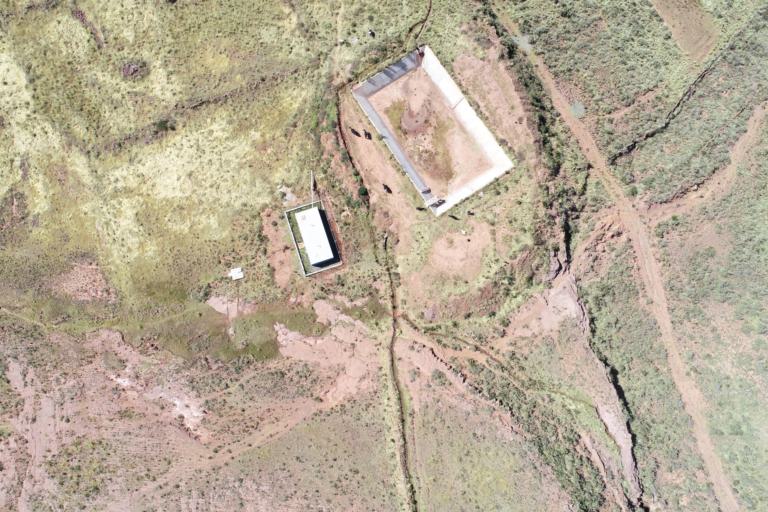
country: BO
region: La Paz
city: Tiahuanaco
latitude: -16.6093
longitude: -68.7673
